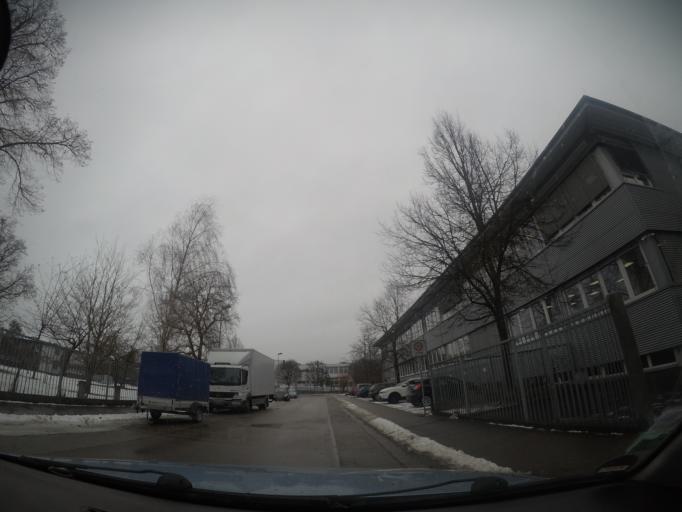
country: DE
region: Bavaria
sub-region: Swabia
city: Neu-Ulm
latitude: 48.3856
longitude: 10.0006
